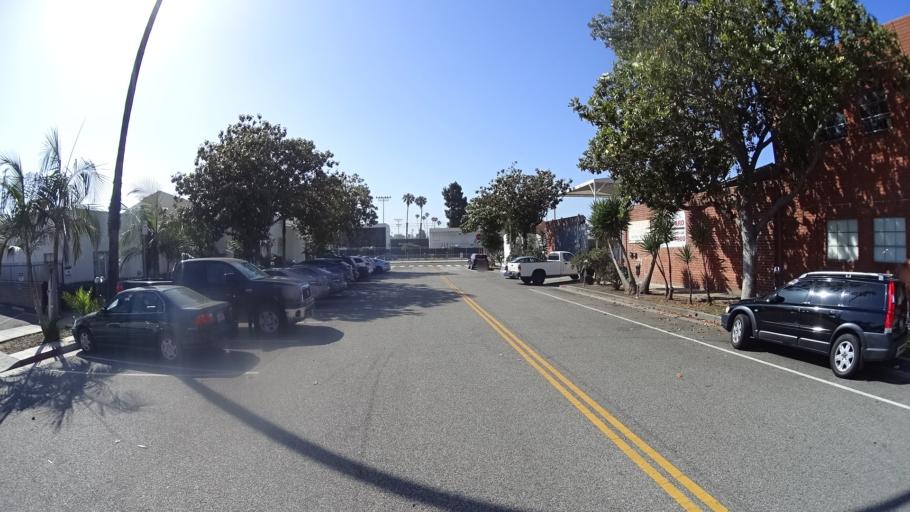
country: US
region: California
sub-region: Los Angeles County
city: Santa Monica
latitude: 34.0226
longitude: -118.4821
